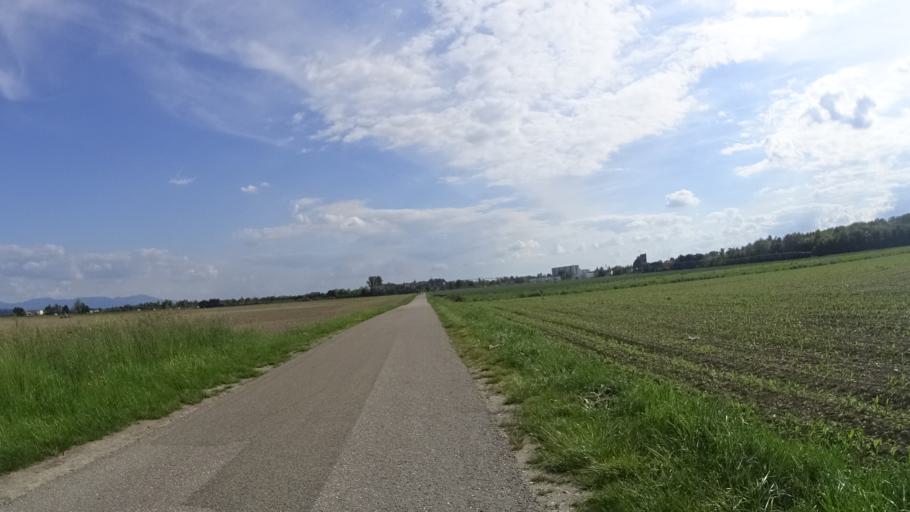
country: DE
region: Baden-Wuerttemberg
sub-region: Freiburg Region
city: Breisach am Rhein
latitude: 48.0540
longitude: 7.5866
